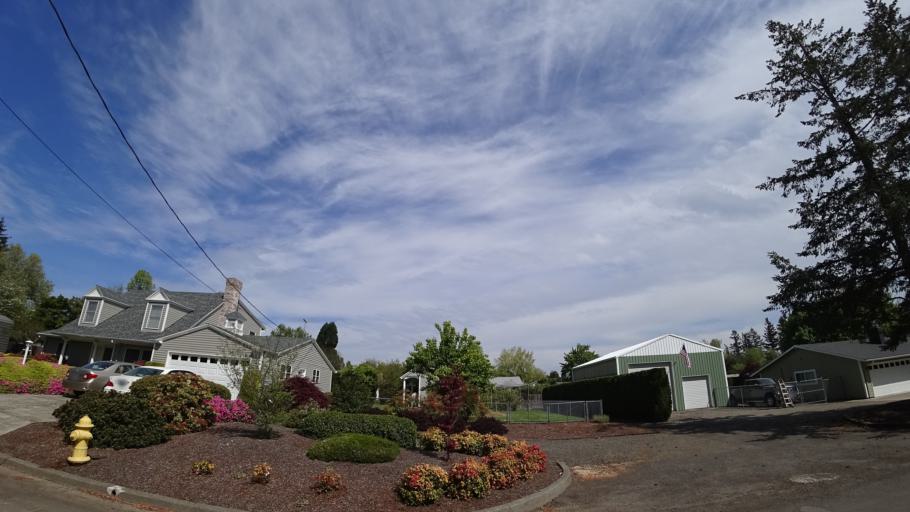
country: US
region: Oregon
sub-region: Washington County
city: Aloha
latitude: 45.4852
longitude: -122.8855
